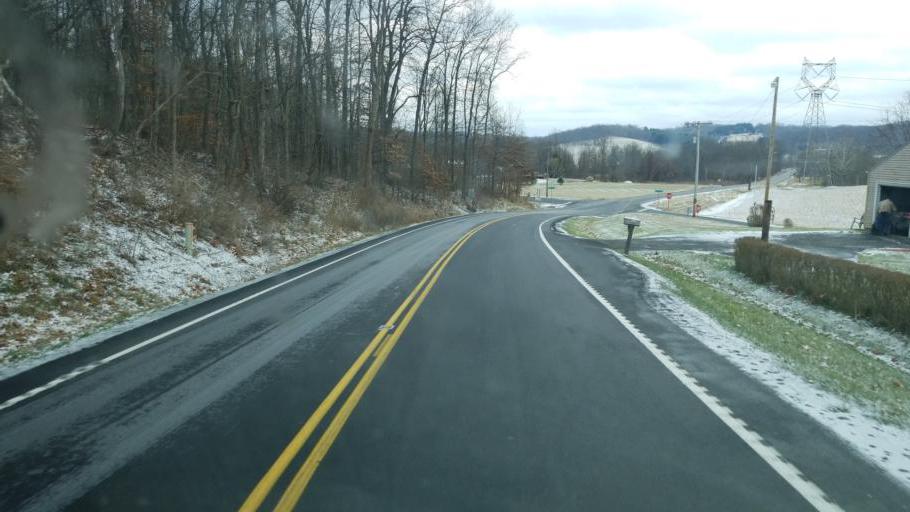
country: US
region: Ohio
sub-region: Muskingum County
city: Frazeysburg
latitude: 40.1389
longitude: -82.2087
